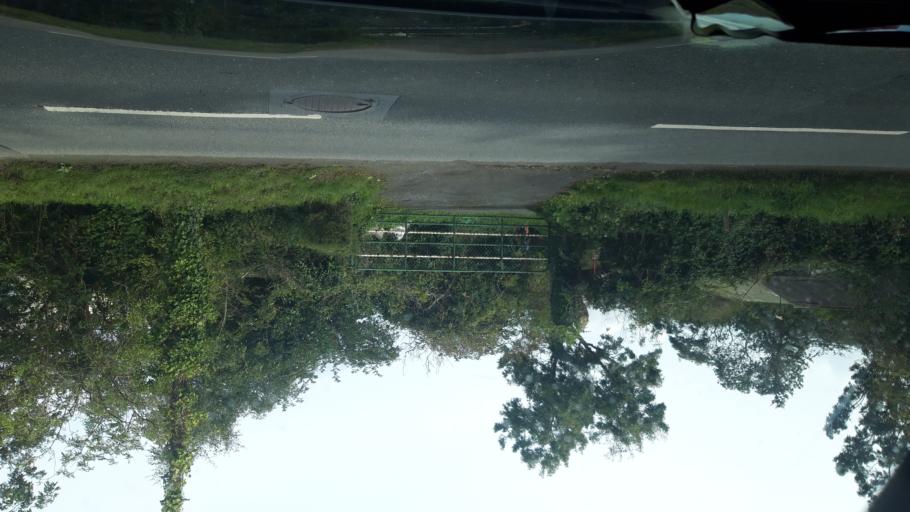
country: IE
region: Leinster
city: Foxrock
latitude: 53.2486
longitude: -6.1814
